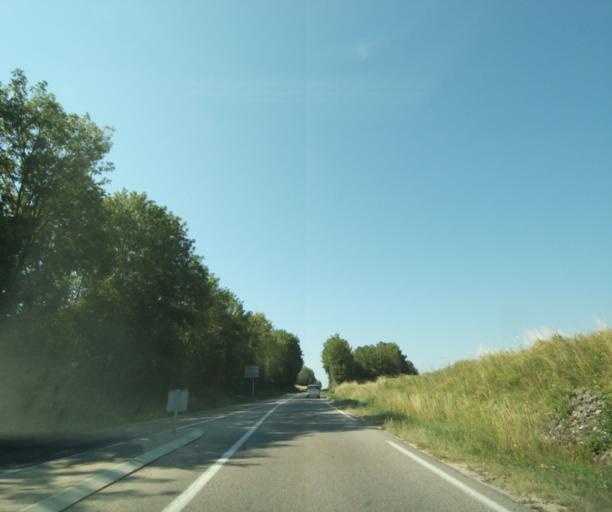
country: FR
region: Lorraine
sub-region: Departement de Meurthe-et-Moselle
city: Toul
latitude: 48.6606
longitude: 5.8772
